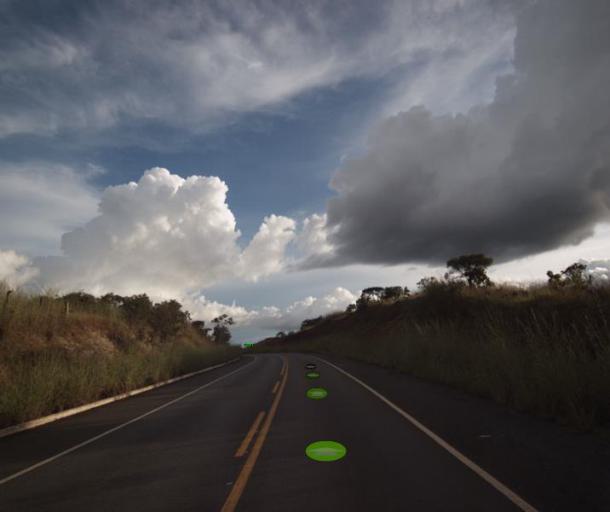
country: BR
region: Goias
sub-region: Niquelandia
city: Niquelandia
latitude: -14.6134
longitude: -48.5908
